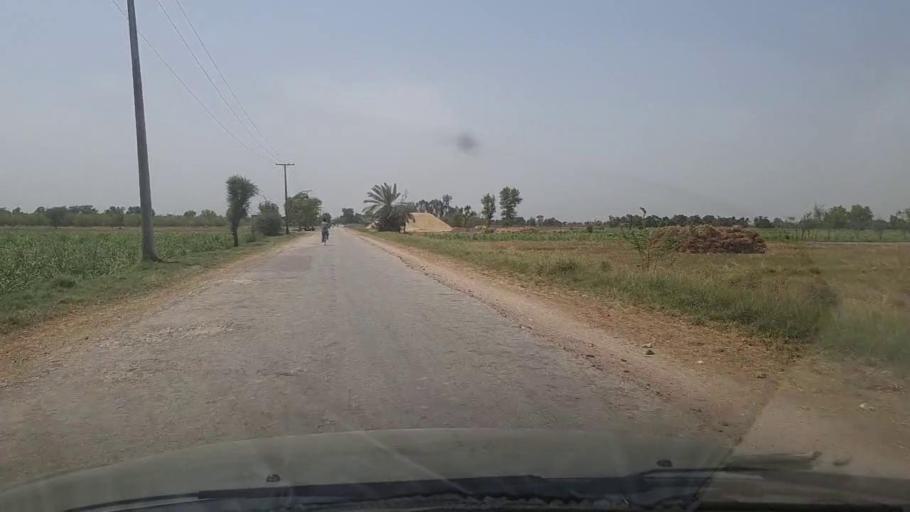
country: PK
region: Sindh
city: Bhiria
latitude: 26.8943
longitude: 68.2421
